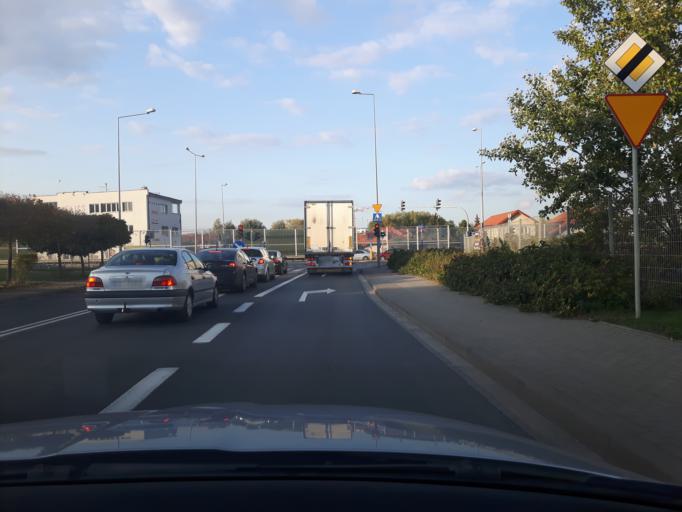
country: PL
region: Masovian Voivodeship
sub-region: Warszawa
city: Wlochy
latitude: 52.1559
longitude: 20.9947
